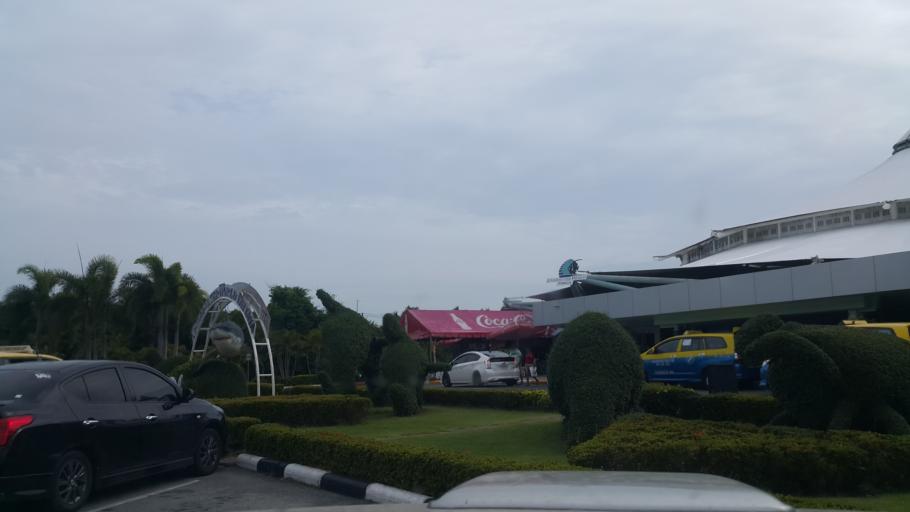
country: TH
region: Chon Buri
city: Phatthaya
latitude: 12.8970
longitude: 100.8966
